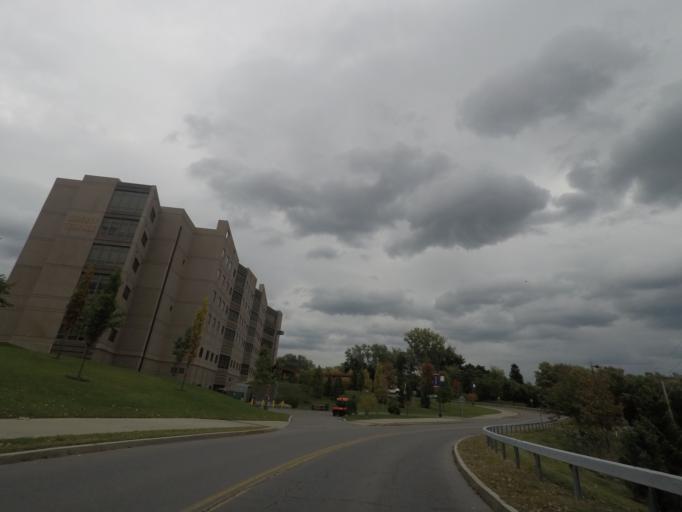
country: US
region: New York
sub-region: Albany County
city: Roessleville
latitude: 42.6781
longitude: -73.8219
